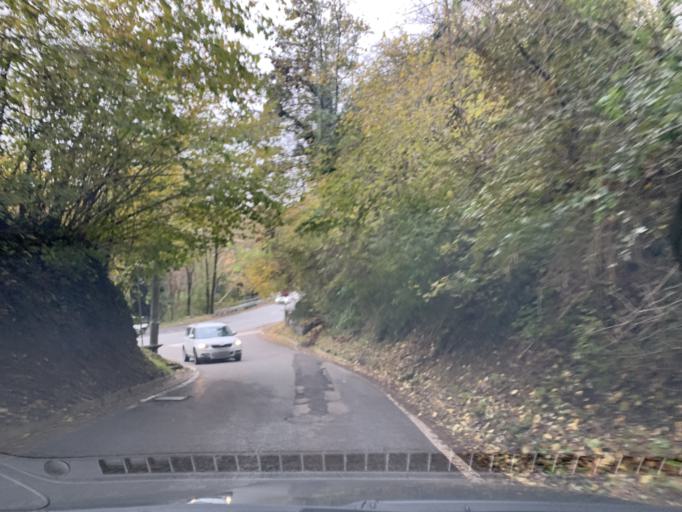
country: IT
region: Lombardy
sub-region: Provincia di Como
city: Casnate Con Bernate
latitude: 45.7434
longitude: 9.0664
